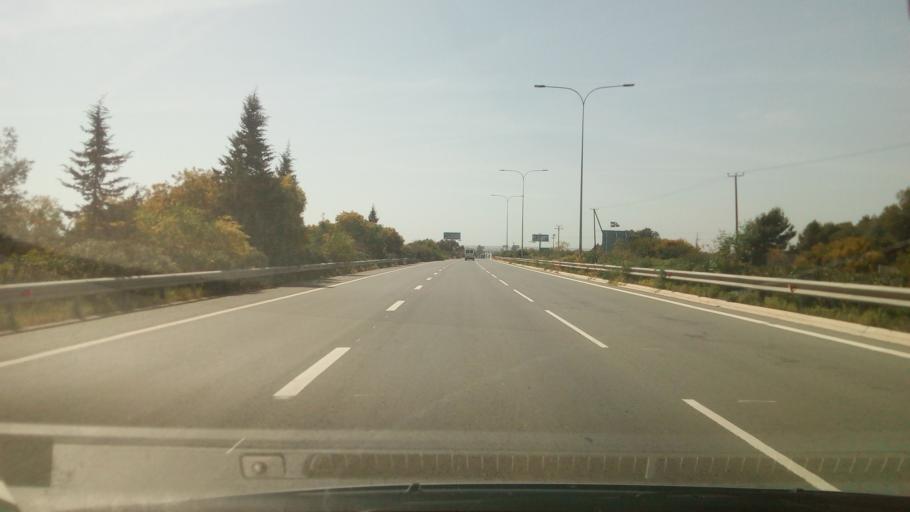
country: CY
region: Ammochostos
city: Liopetri
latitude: 34.9837
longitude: 33.9246
